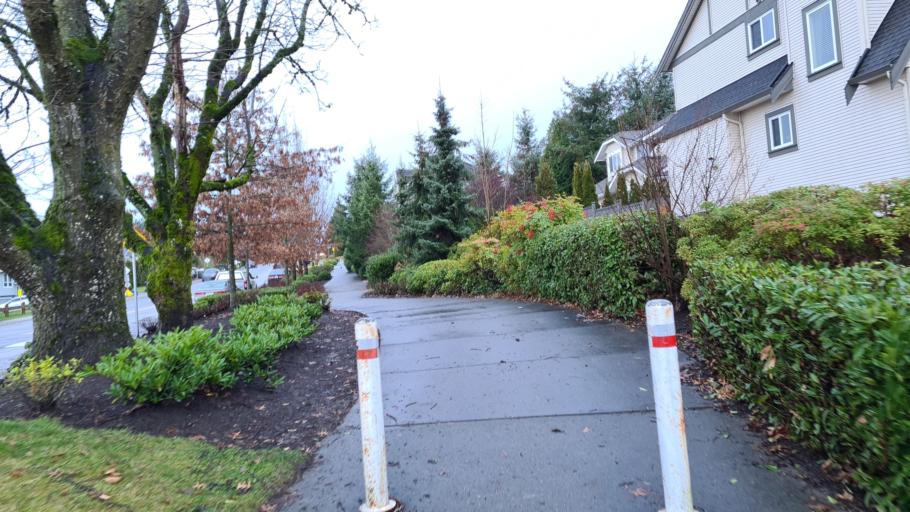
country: CA
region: British Columbia
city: Langley
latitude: 49.1264
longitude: -122.6704
